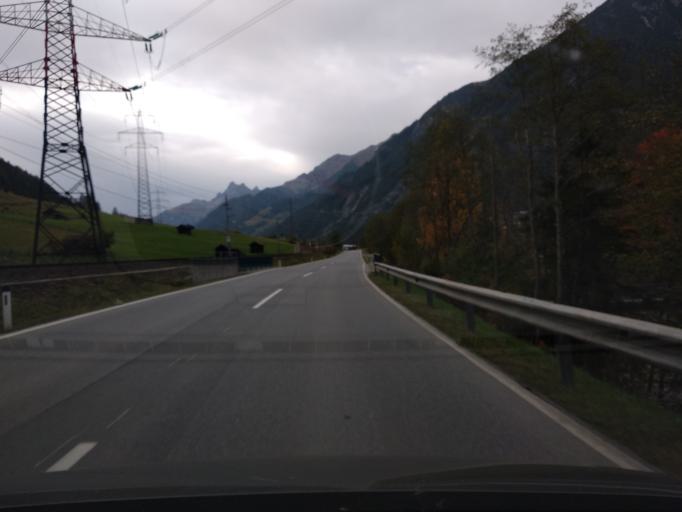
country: AT
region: Tyrol
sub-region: Politischer Bezirk Landeck
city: Flirsch
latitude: 47.1492
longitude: 10.3883
